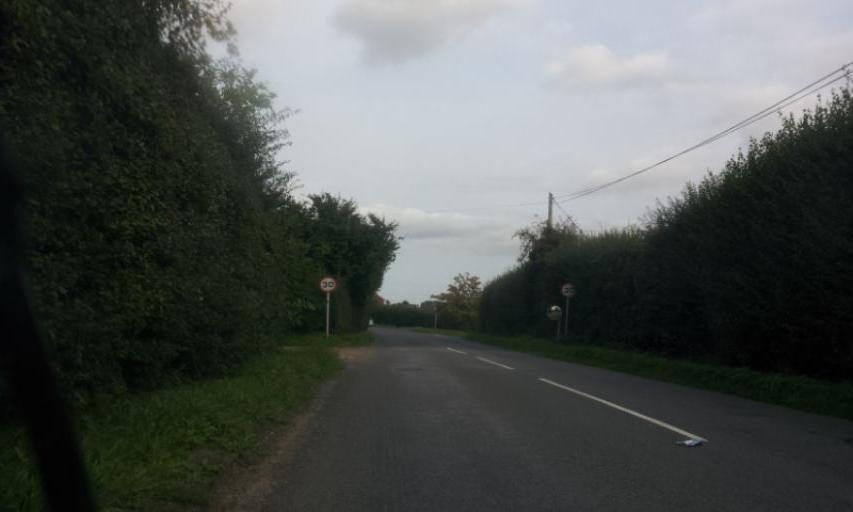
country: GB
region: England
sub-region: Kent
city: Hadlow
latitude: 51.2104
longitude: 0.3404
